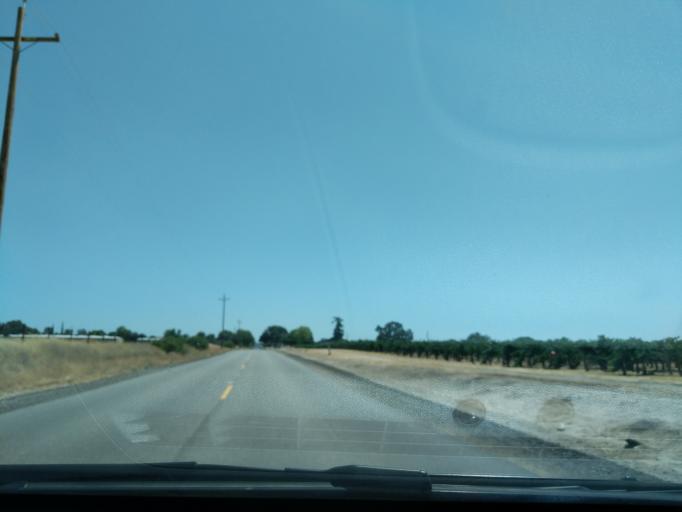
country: US
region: California
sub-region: San Luis Obispo County
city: Paso Robles
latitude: 35.6804
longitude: -120.6409
